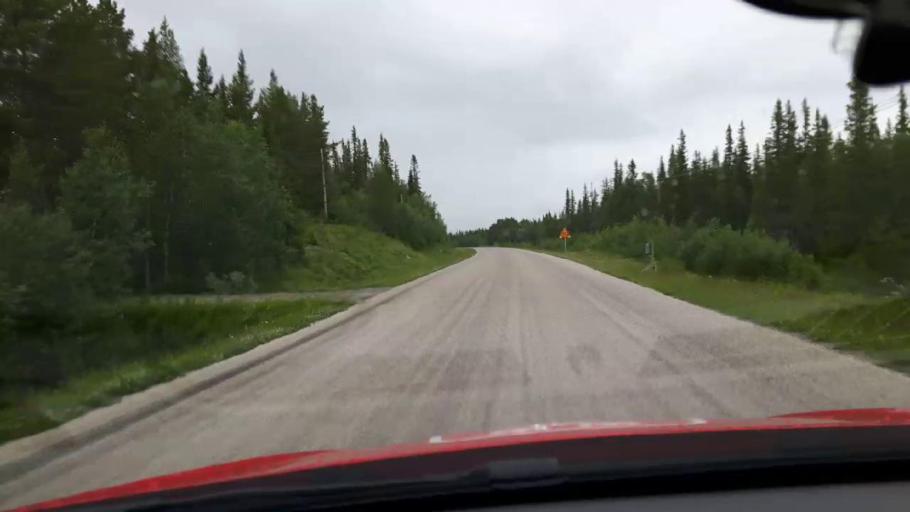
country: NO
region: Nord-Trondelag
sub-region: Meraker
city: Meraker
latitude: 63.2658
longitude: 12.3929
